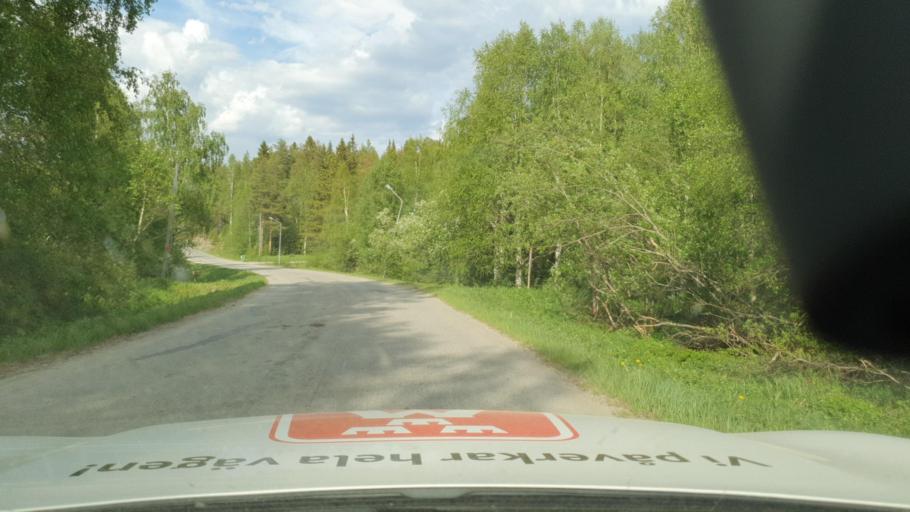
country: SE
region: Vaesterbotten
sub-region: Vindelns Kommun
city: Vindeln
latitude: 64.0948
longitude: 19.6743
